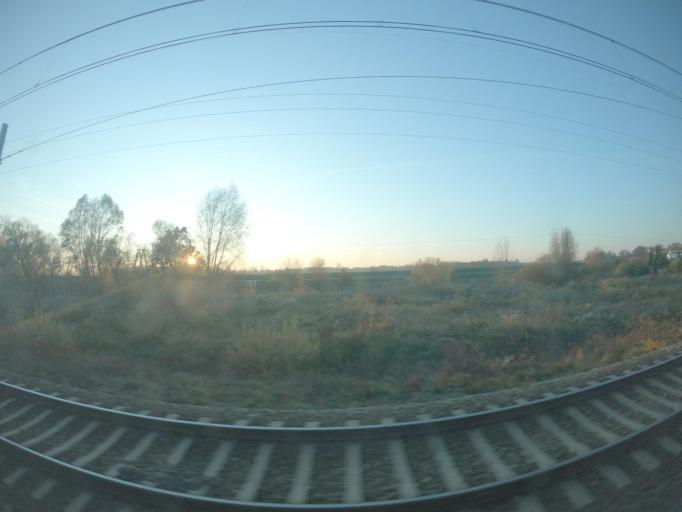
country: PL
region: Lubusz
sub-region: Powiat gorzowski
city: Kostrzyn nad Odra
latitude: 52.5734
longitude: 14.6438
